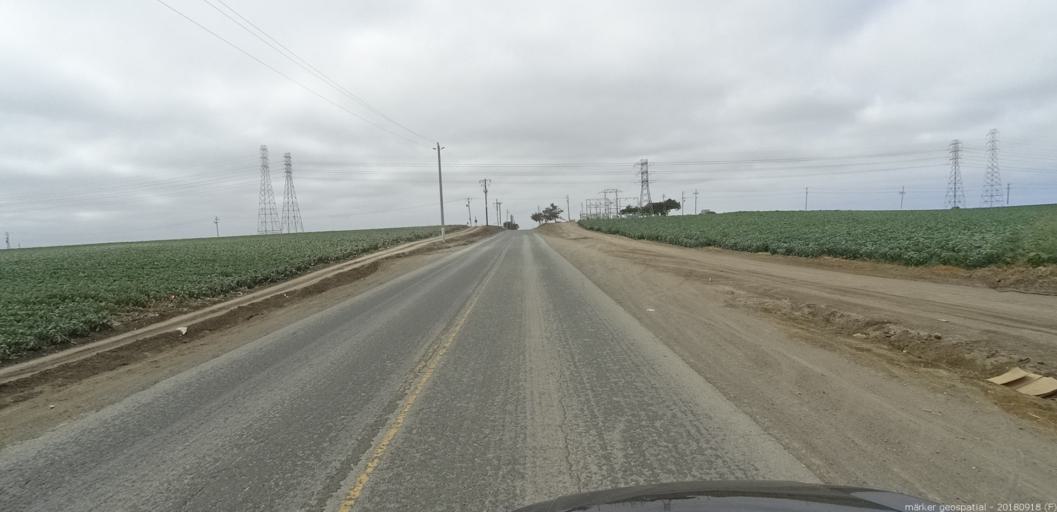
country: US
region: California
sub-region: Monterey County
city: Castroville
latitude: 36.7637
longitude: -121.7319
